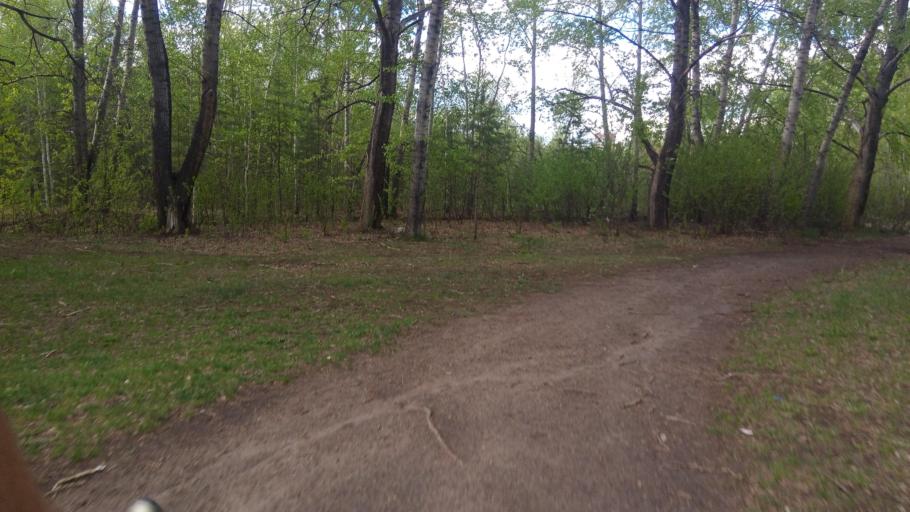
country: RU
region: Chelyabinsk
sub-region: Gorod Chelyabinsk
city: Chelyabinsk
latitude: 55.1680
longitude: 61.3414
